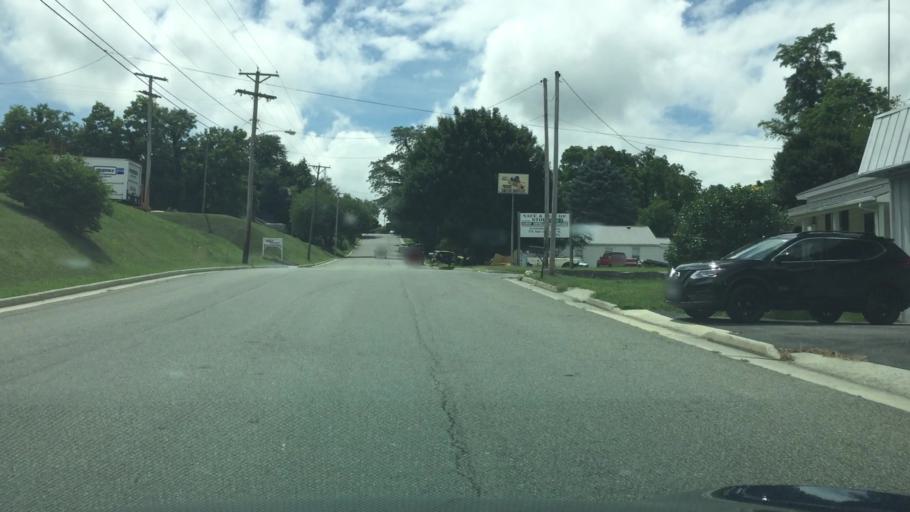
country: US
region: Virginia
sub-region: Wythe County
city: Wytheville
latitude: 36.9485
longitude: -81.0670
